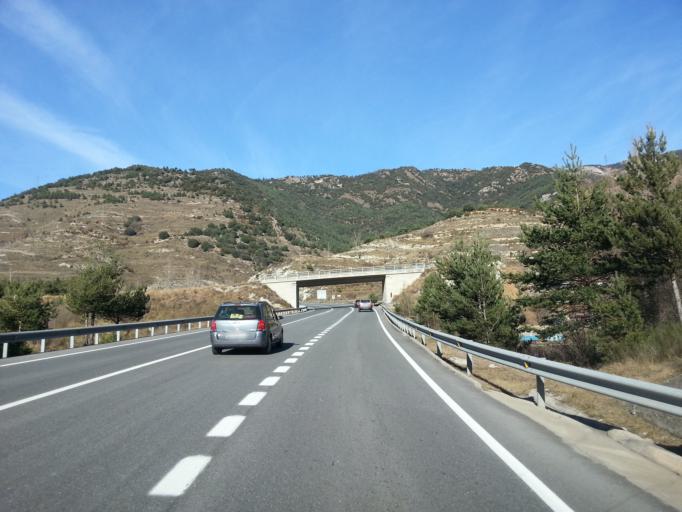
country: ES
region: Catalonia
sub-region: Provincia de Barcelona
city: Baga
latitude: 42.2553
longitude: 1.8655
